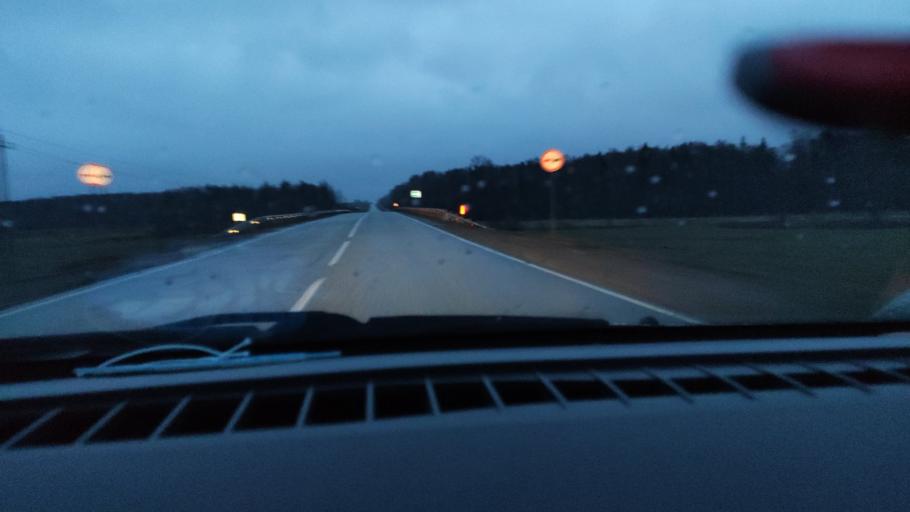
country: RU
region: Udmurtiya
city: Mozhga
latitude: 56.3630
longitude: 52.2572
